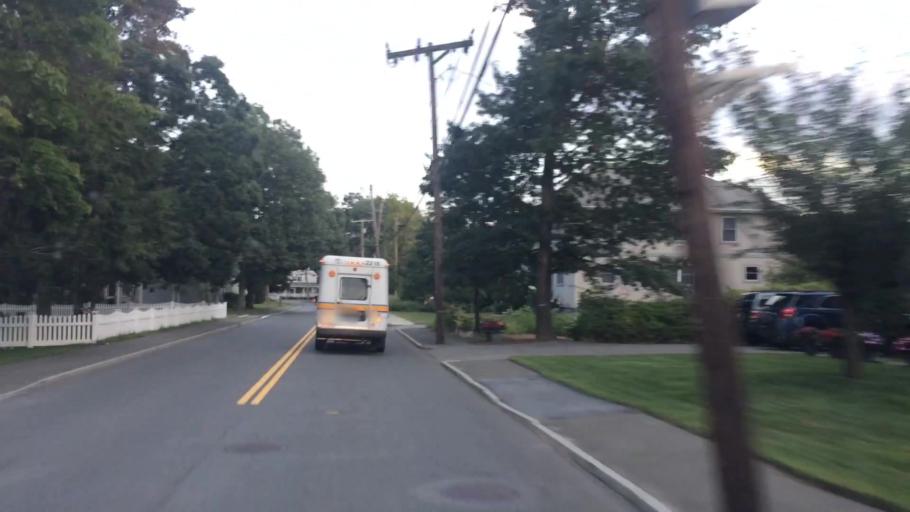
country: US
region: Massachusetts
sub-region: Middlesex County
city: Woburn
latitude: 42.4872
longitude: -71.1293
